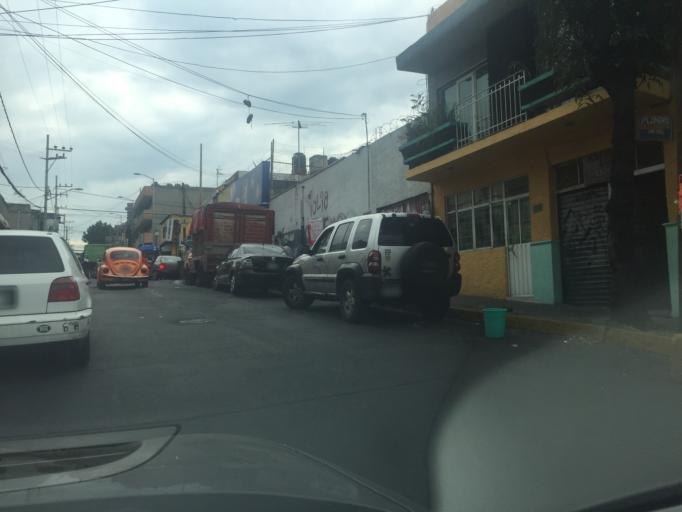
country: MX
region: Mexico City
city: Alvaro Obregon
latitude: 19.3726
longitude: -99.2142
